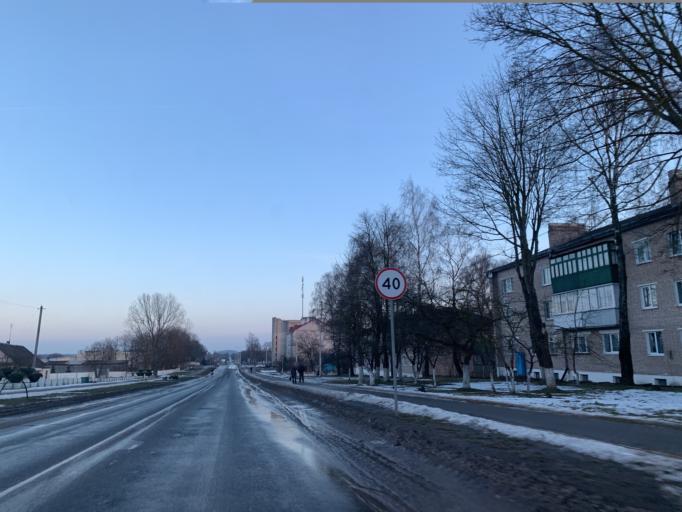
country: BY
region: Minsk
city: Nyasvizh
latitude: 53.2316
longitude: 26.6551
